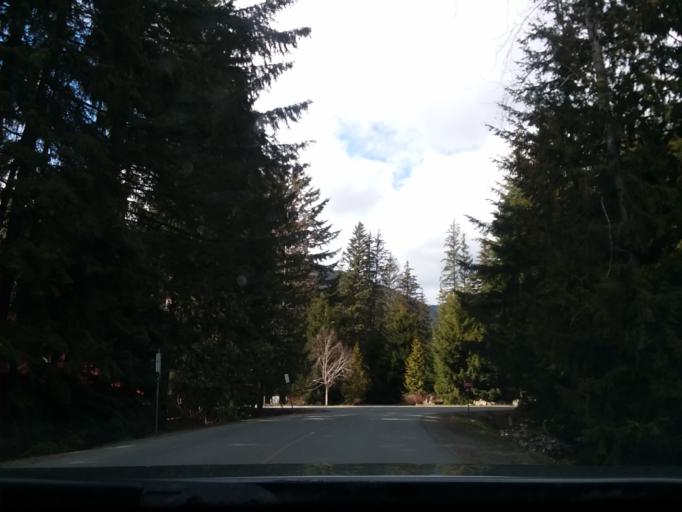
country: CA
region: British Columbia
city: Whistler
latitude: 50.1231
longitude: -122.9712
